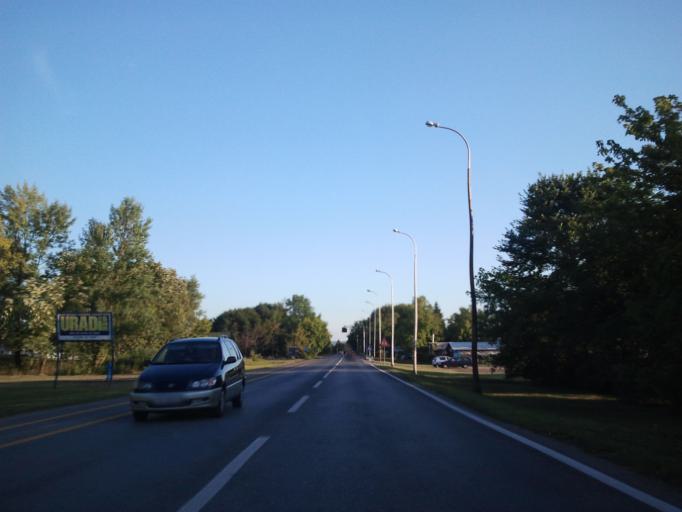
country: HR
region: Sisacko-Moslavacka
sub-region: Grad Sisak
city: Sisak
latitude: 45.4591
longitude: 16.3715
